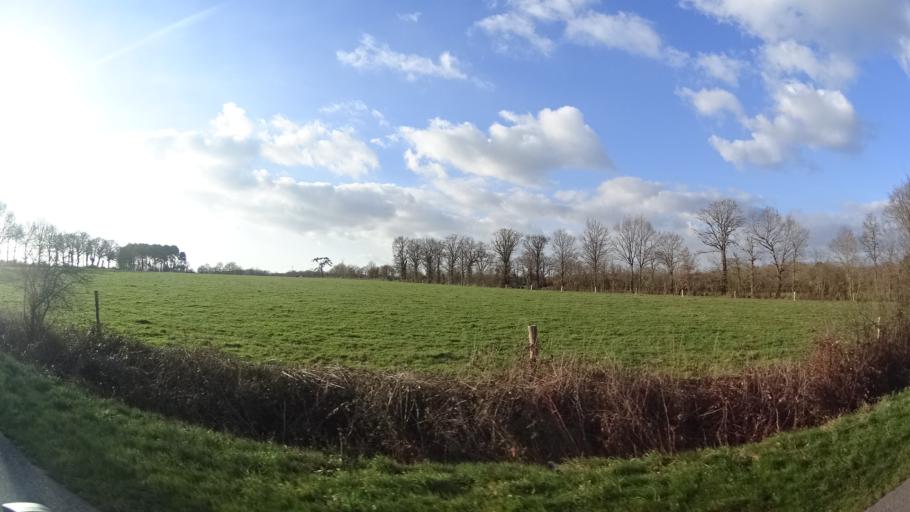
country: FR
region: Pays de la Loire
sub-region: Departement de la Loire-Atlantique
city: Plesse
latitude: 47.5704
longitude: -1.8671
